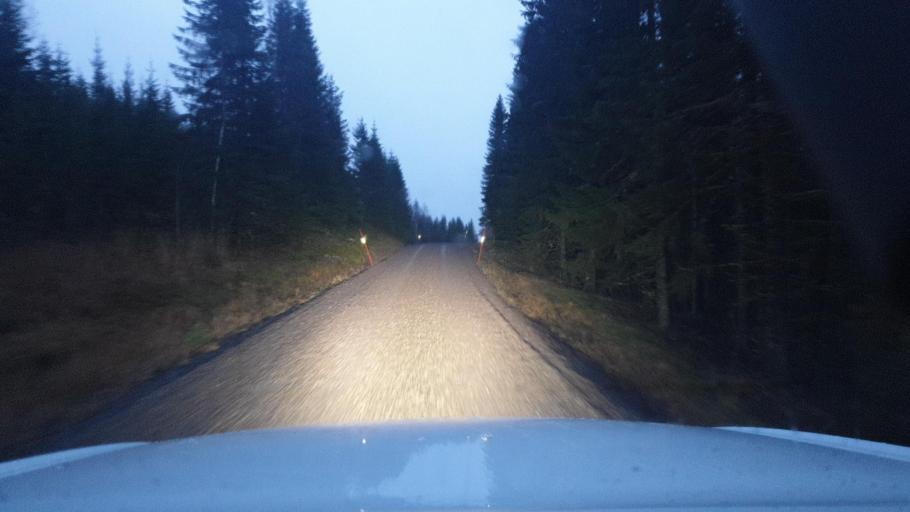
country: SE
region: Vaermland
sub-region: Eda Kommun
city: Charlottenberg
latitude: 60.1003
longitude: 12.6094
